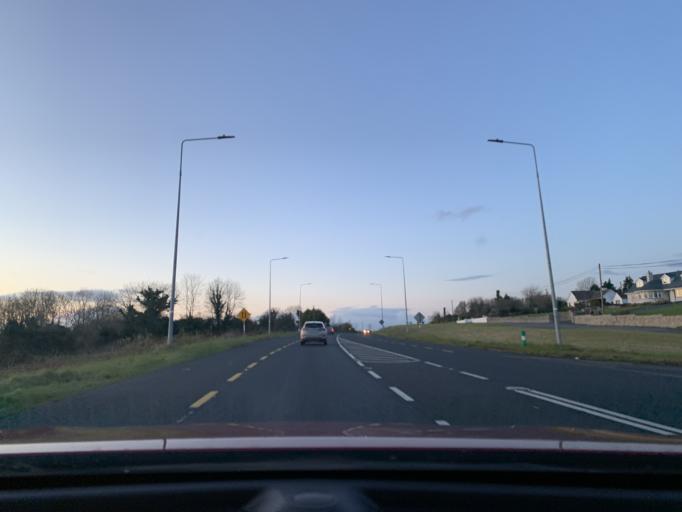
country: IE
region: Connaught
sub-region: County Leitrim
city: Carrick-on-Shannon
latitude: 53.8840
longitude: -7.9390
